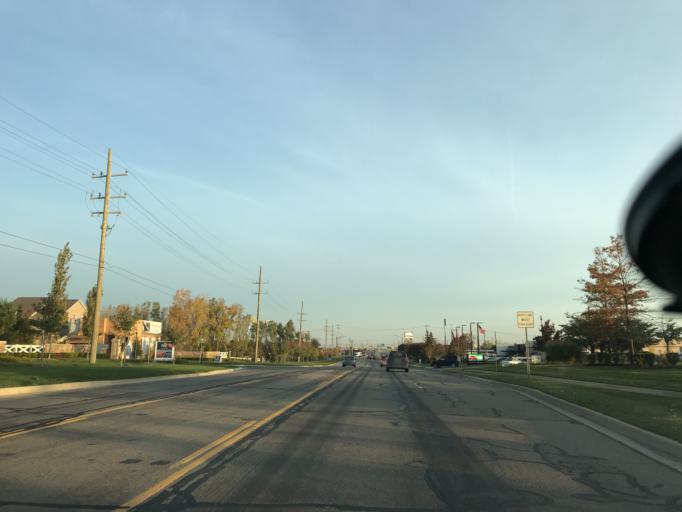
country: US
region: Michigan
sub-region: Oakland County
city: Wixom
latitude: 42.4910
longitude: -83.5356
